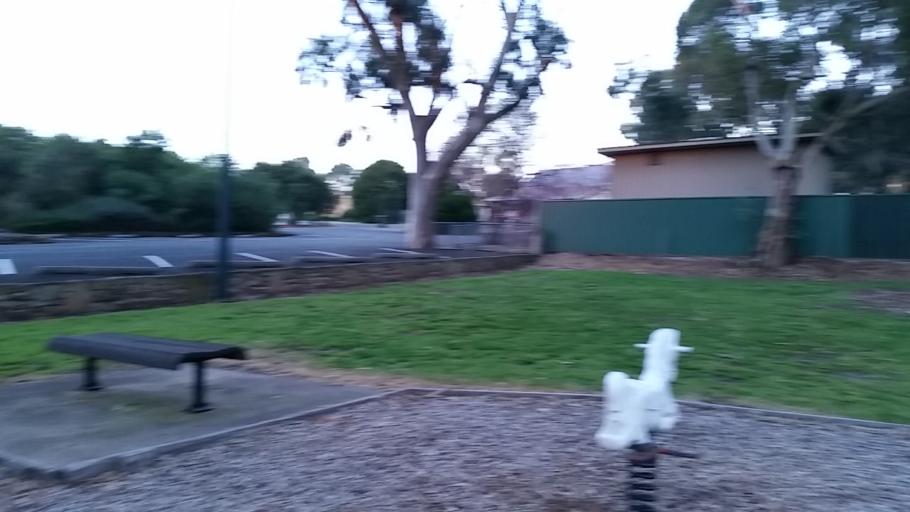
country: AU
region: South Australia
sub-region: Barossa
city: Williamstown
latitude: -34.6702
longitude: 138.8910
